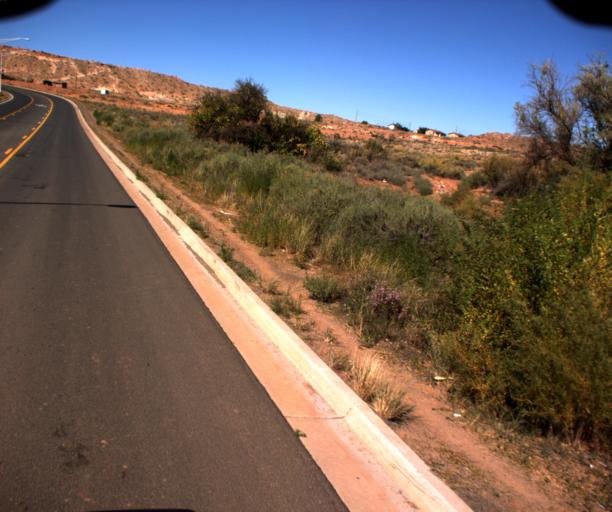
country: US
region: Arizona
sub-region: Coconino County
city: Tuba City
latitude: 36.1115
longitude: -111.2196
